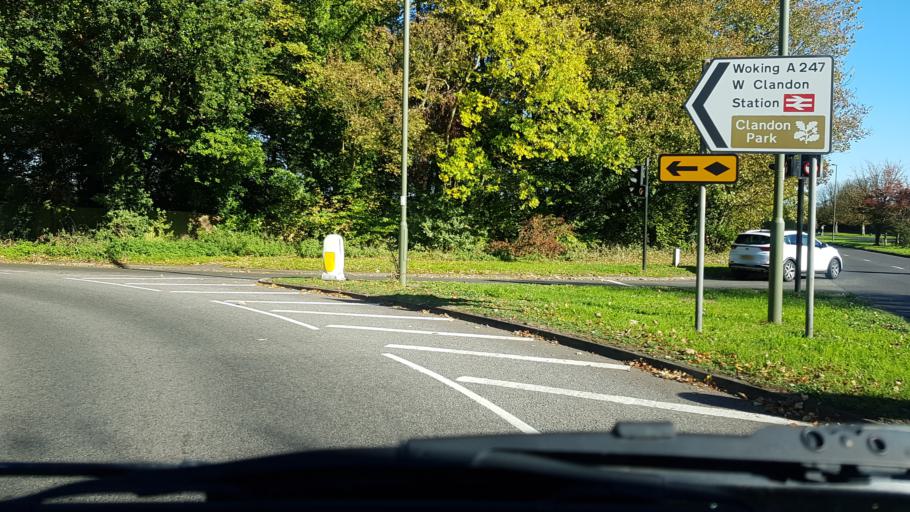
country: GB
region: England
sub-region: Surrey
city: Chilworth
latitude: 51.2489
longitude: -0.5035
